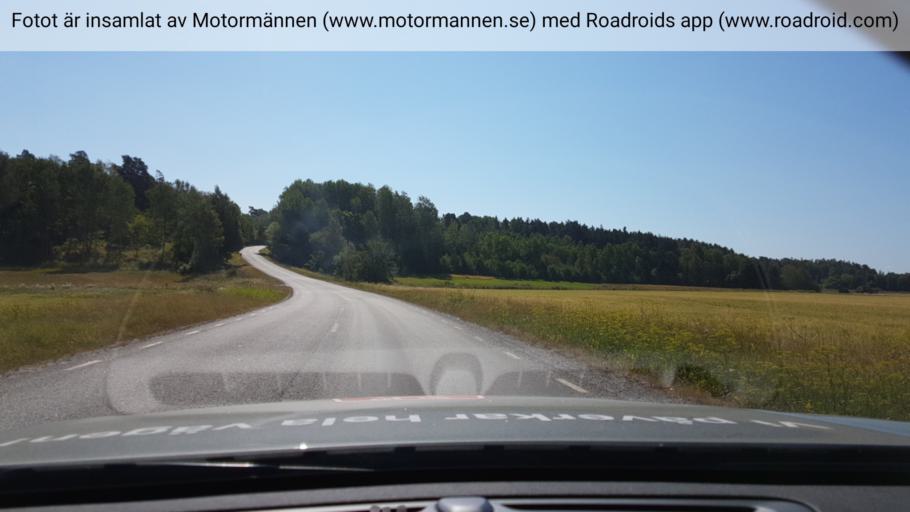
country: SE
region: Stockholm
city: Stenhamra
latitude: 59.3918
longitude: 17.5718
